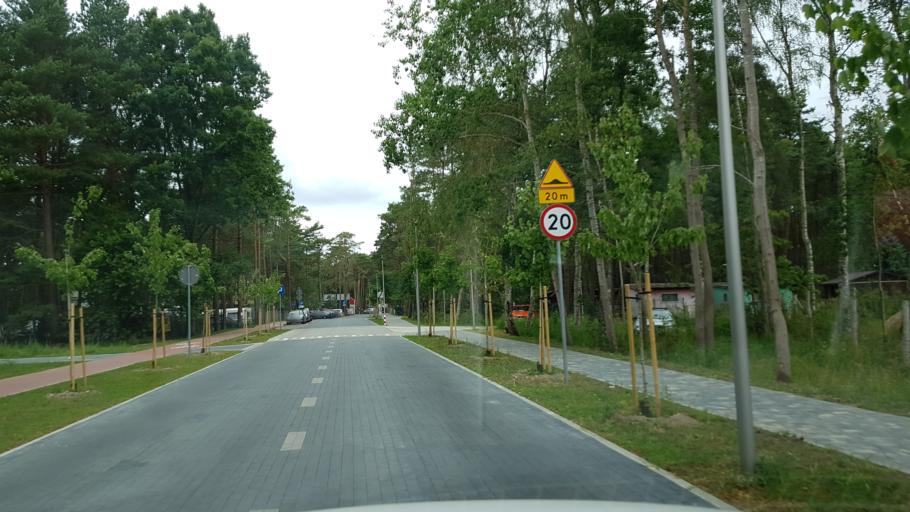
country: PL
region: West Pomeranian Voivodeship
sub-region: Powiat kamienski
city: Dziwnow
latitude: 54.0028
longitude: 14.6857
